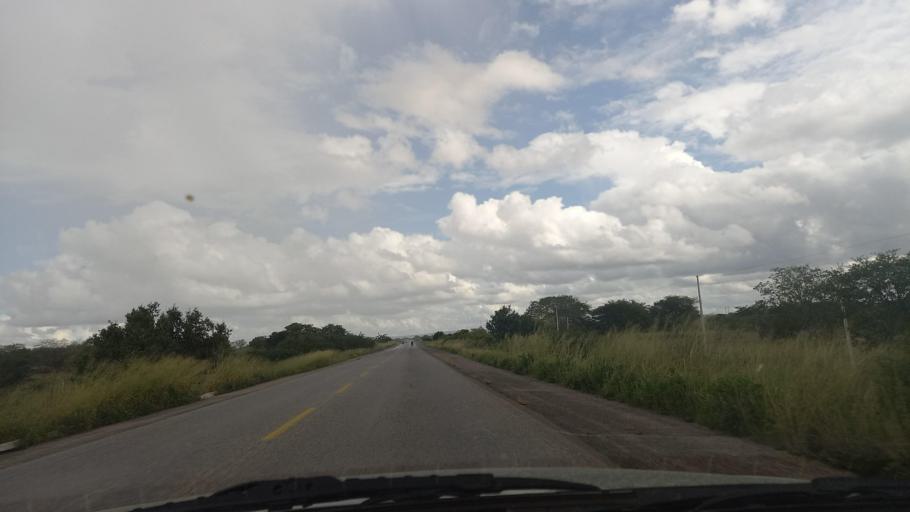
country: BR
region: Pernambuco
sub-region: Cachoeirinha
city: Cachoeirinha
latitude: -8.5482
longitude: -36.2715
